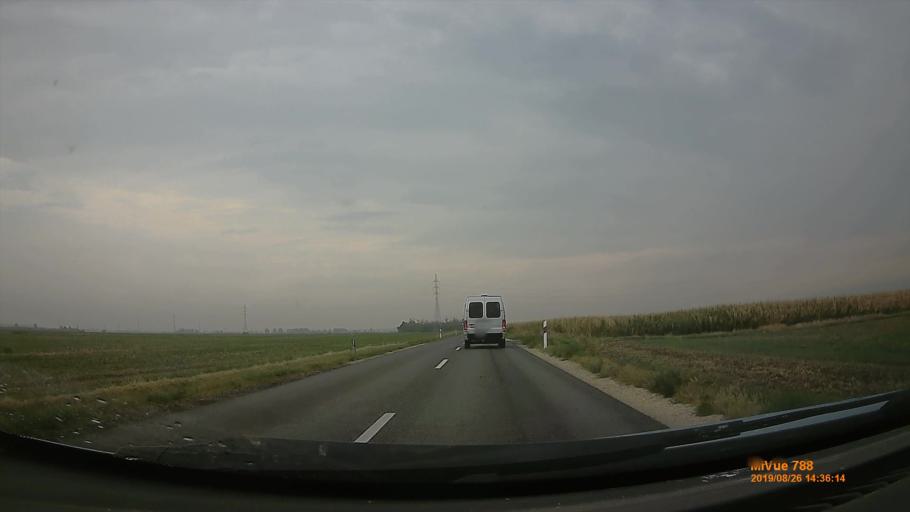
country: HU
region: Fejer
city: Szekesfehervar
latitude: 47.2403
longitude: 18.4177
